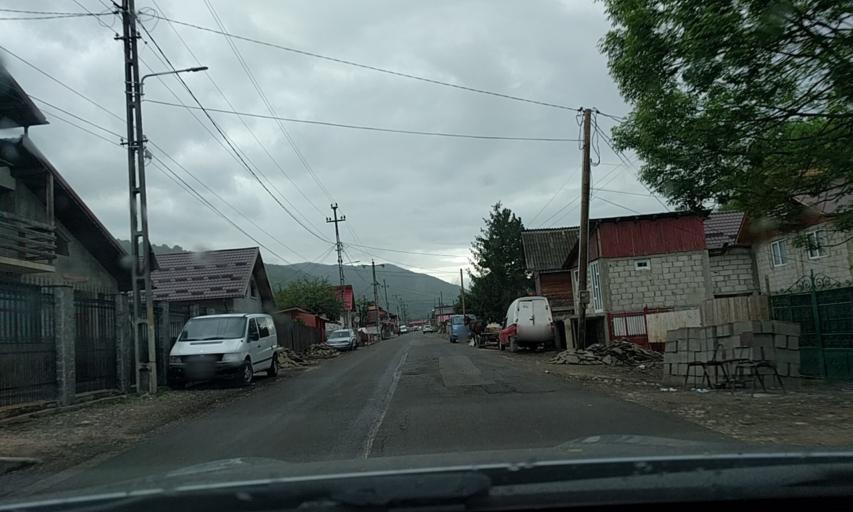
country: RO
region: Dambovita
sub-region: Comuna Moroeni
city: Glod
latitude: 45.2372
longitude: 25.4457
